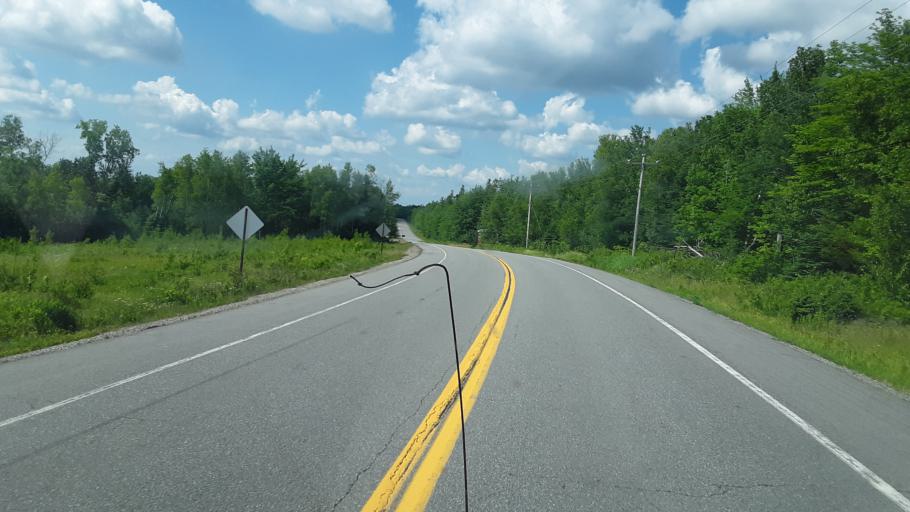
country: US
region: Maine
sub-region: Washington County
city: Machias
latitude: 45.0032
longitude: -67.5528
